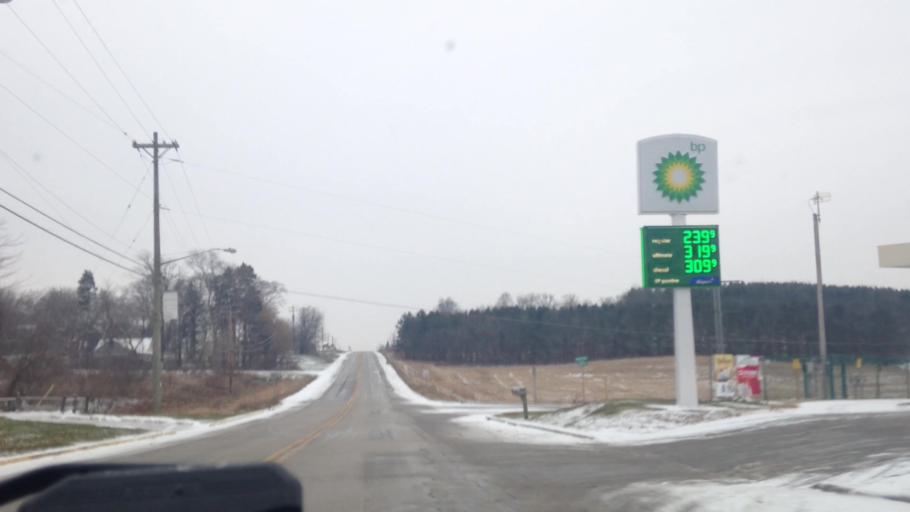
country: US
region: Wisconsin
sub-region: Dodge County
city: Hustisford
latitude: 43.3069
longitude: -88.5184
